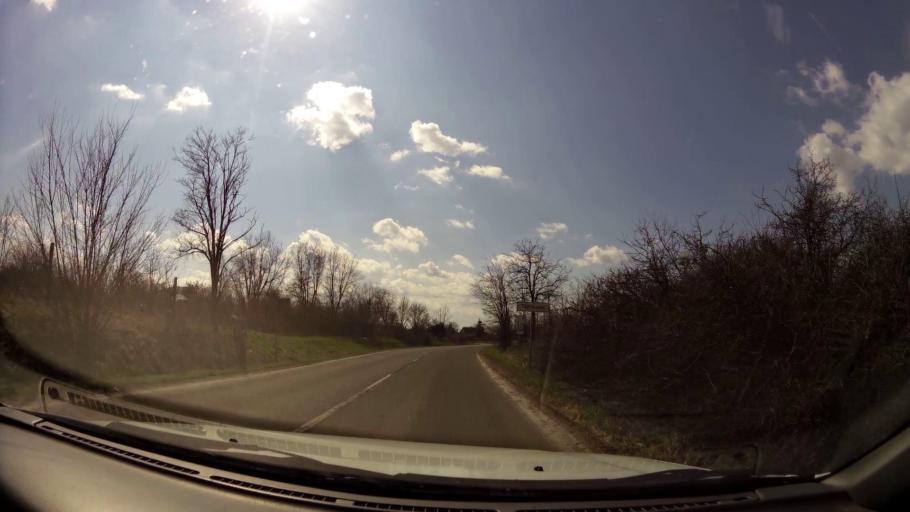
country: HU
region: Pest
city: Tapioszele
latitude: 47.3331
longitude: 19.8882
